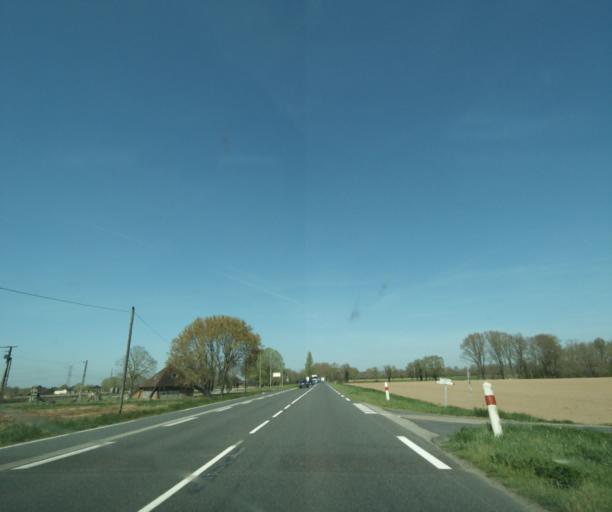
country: FR
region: Bourgogne
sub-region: Departement de la Nievre
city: Chantenay-Saint-Imbert
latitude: 46.6827
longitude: 3.2250
